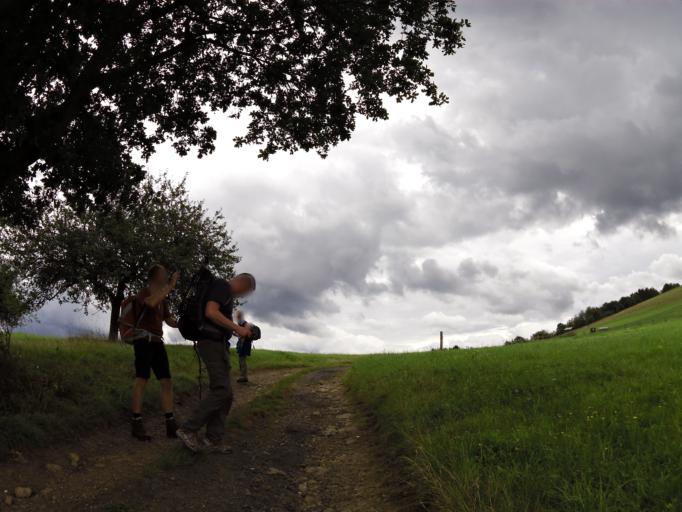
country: DE
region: Rheinland-Pfalz
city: Staudernheim
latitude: 49.7722
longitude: 7.6902
